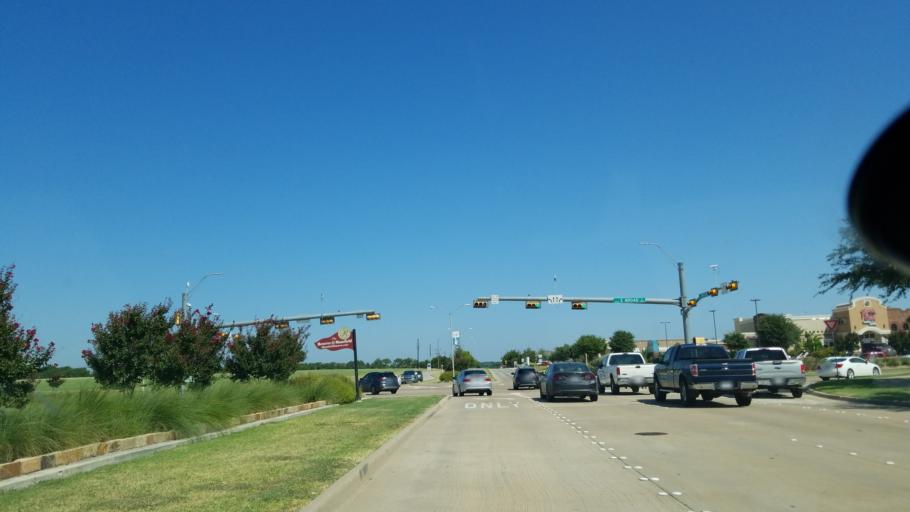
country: US
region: Texas
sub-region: Tarrant County
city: Mansfield
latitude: 32.5680
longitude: -97.0970
